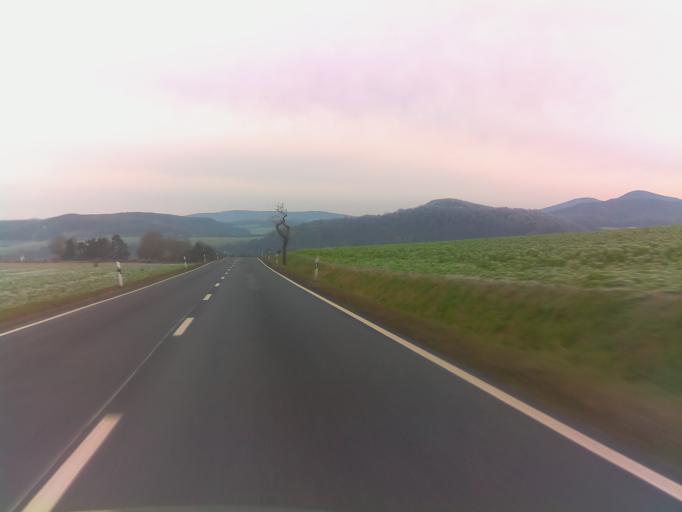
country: DE
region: Thuringia
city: Buttlar
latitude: 50.7738
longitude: 9.9711
